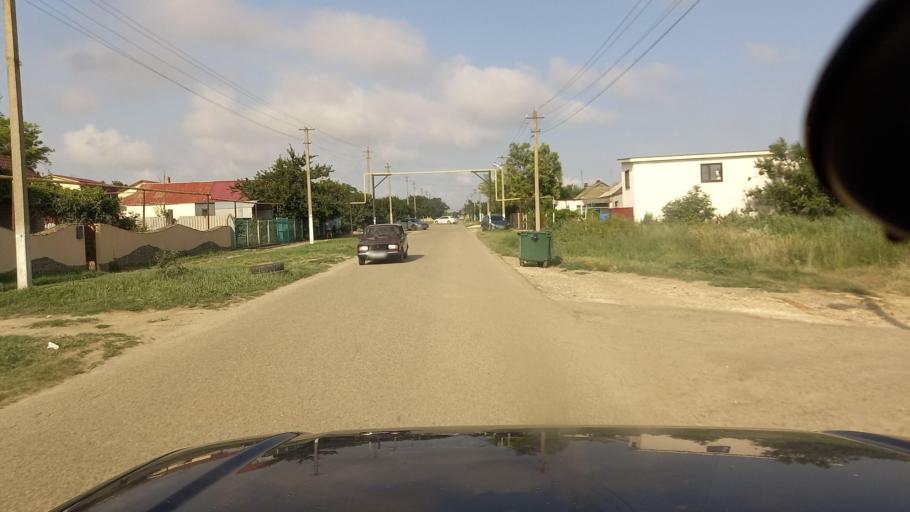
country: RU
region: Krasnodarskiy
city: Vyshestebliyevskaya
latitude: 45.1267
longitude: 36.9014
